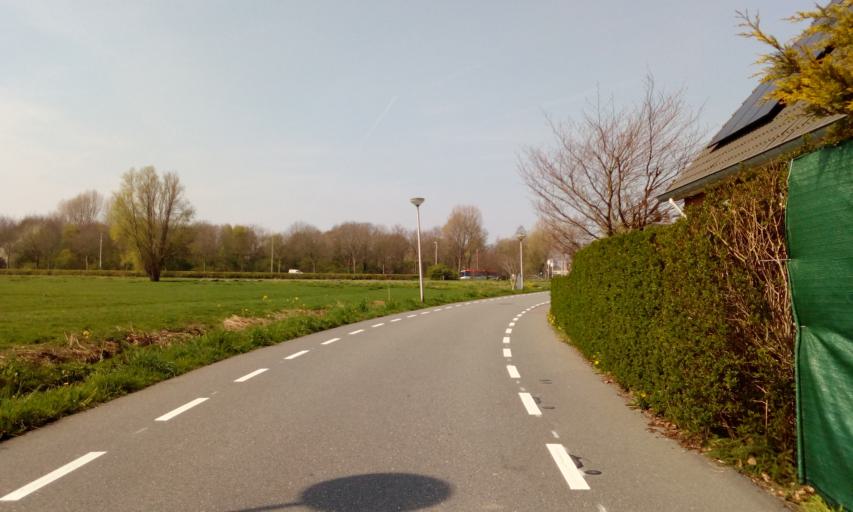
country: NL
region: South Holland
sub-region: Gemeente Spijkenisse
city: Spijkenisse
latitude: 51.8288
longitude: 4.3375
